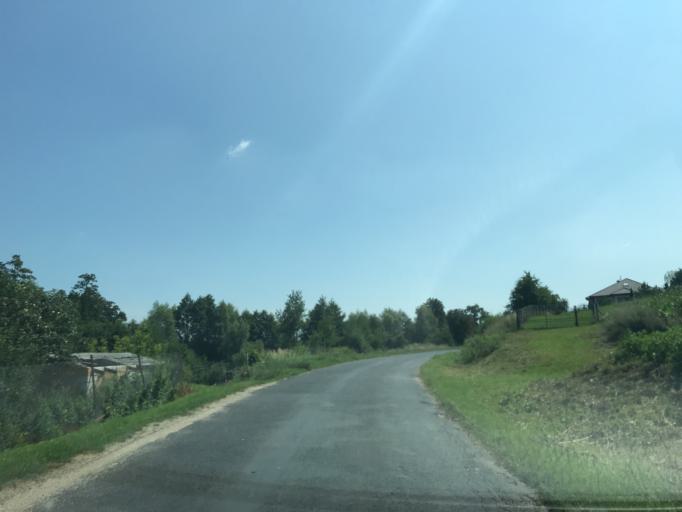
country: PL
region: Kujawsko-Pomorskie
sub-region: Powiat golubsko-dobrzynski
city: Zbojno
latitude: 52.9971
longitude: 19.2096
